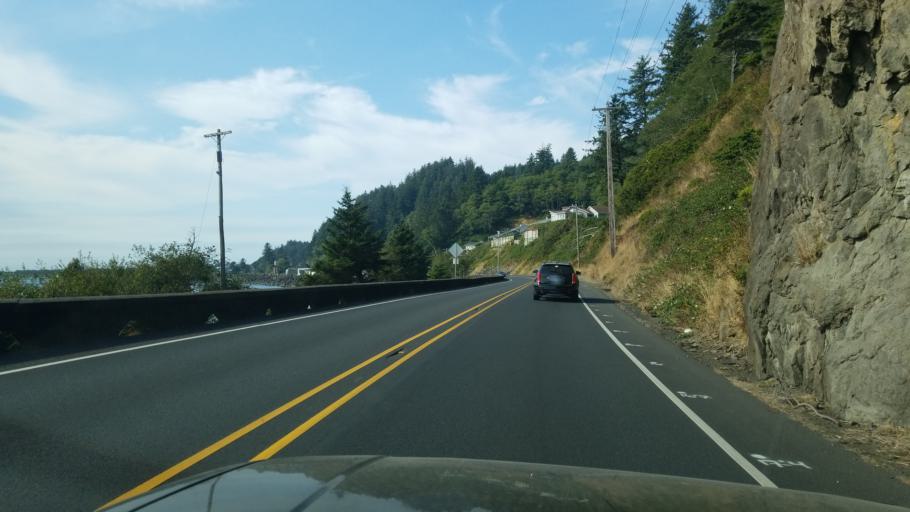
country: US
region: Oregon
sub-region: Tillamook County
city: Rockaway Beach
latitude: 45.5612
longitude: -123.9341
